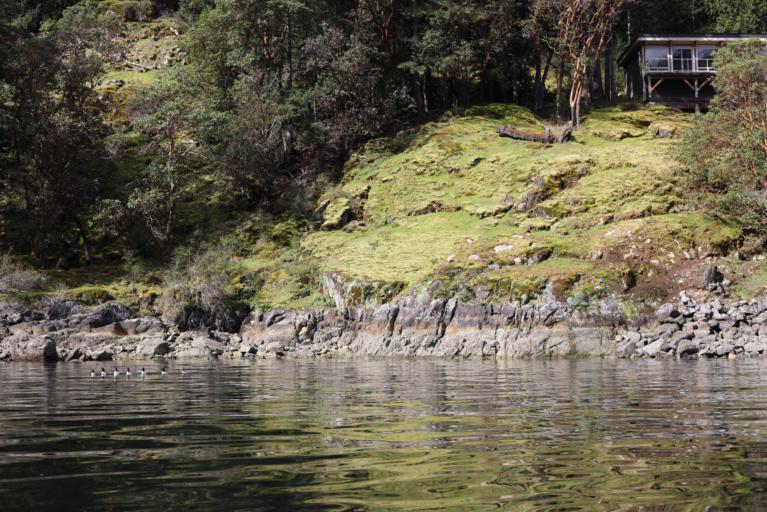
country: CA
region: British Columbia
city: Langford
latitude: 48.5195
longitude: -123.5421
